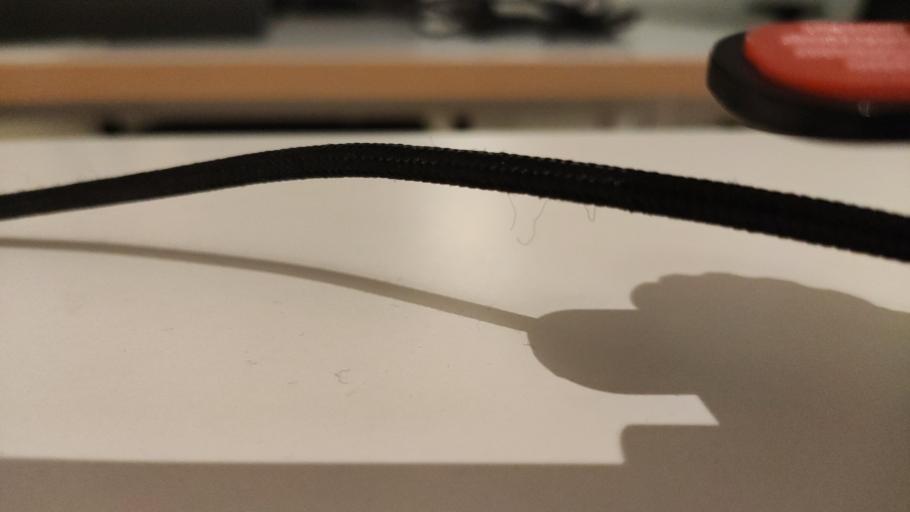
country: RU
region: Moskovskaya
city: Meshcherino
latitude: 55.1878
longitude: 38.3580
